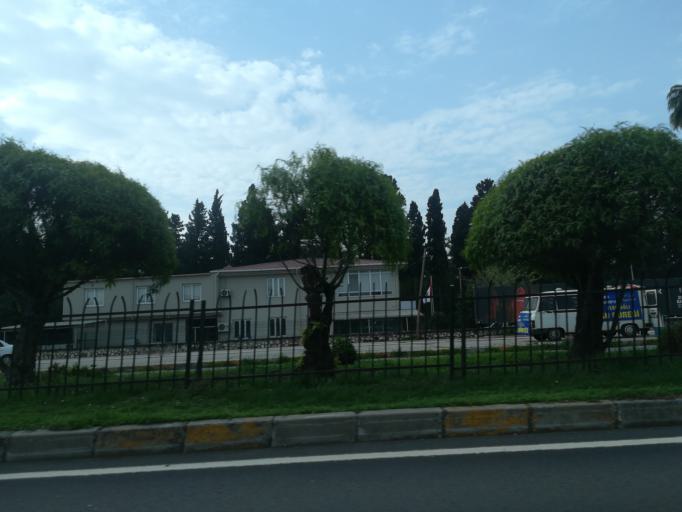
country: TR
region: Adana
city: Yuregir
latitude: 36.9869
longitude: 35.3556
